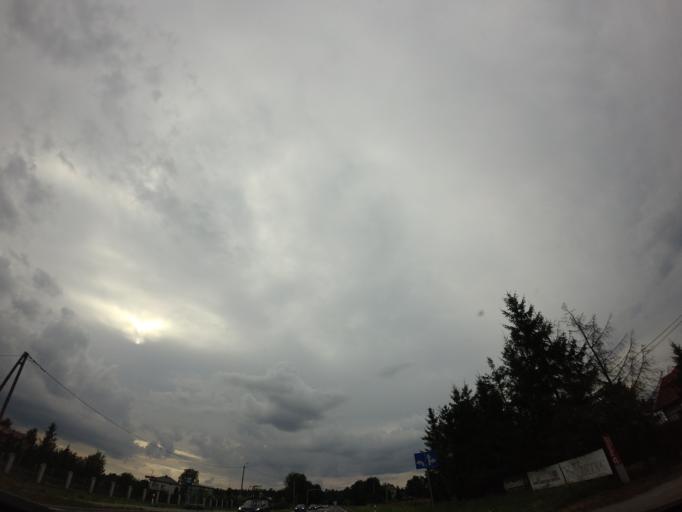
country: PL
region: Masovian Voivodeship
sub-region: Powiat sierpecki
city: Sierpc
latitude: 52.8695
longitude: 19.6472
